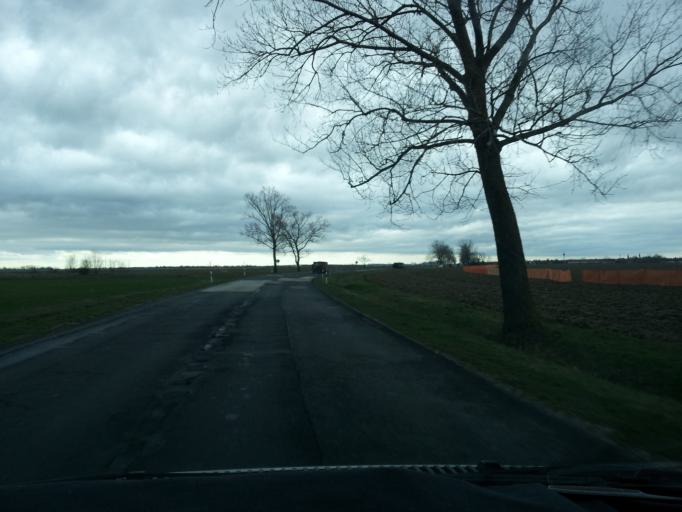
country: HU
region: Gyor-Moson-Sopron
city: Beled
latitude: 47.4742
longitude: 17.1330
